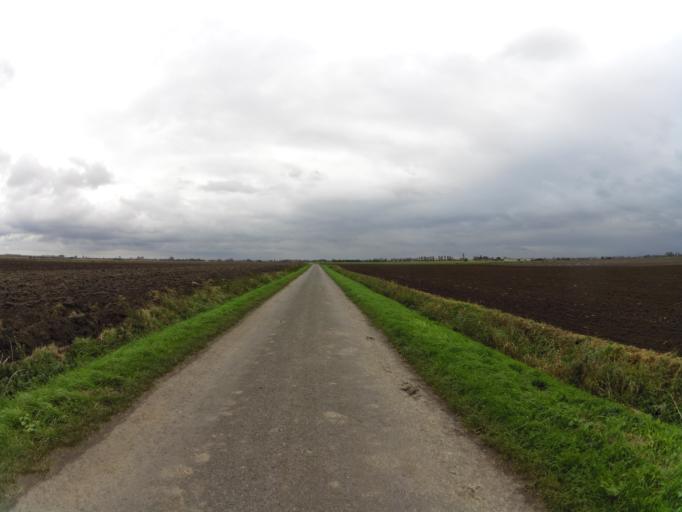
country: BE
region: Flanders
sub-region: Provincie West-Vlaanderen
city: Gistel
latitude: 51.1336
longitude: 2.9236
